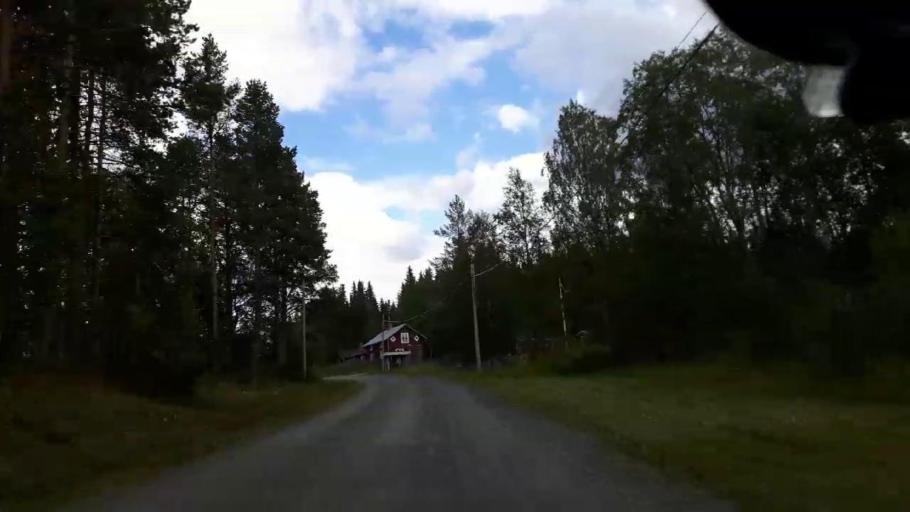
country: SE
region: Jaemtland
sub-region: Stroemsunds Kommun
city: Stroemsund
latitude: 63.4198
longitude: 15.8387
